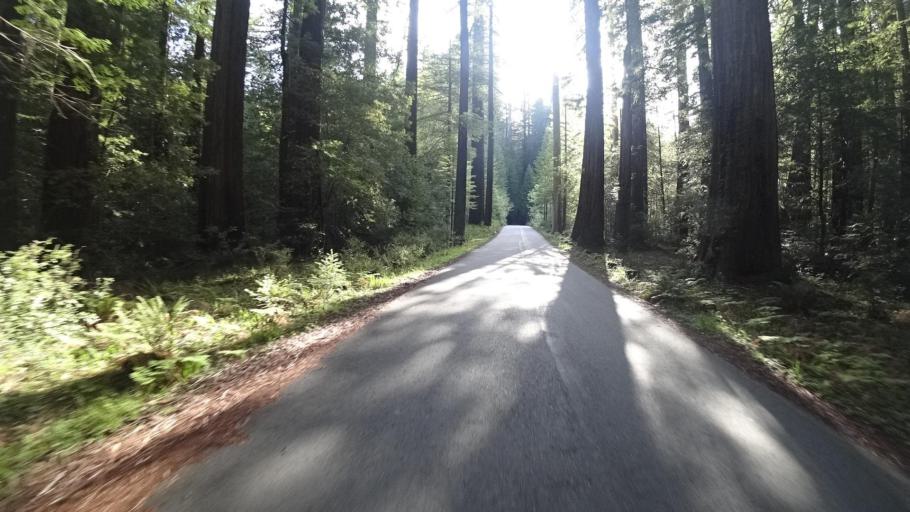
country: US
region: California
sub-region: Humboldt County
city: Rio Dell
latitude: 40.3511
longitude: -124.0064
